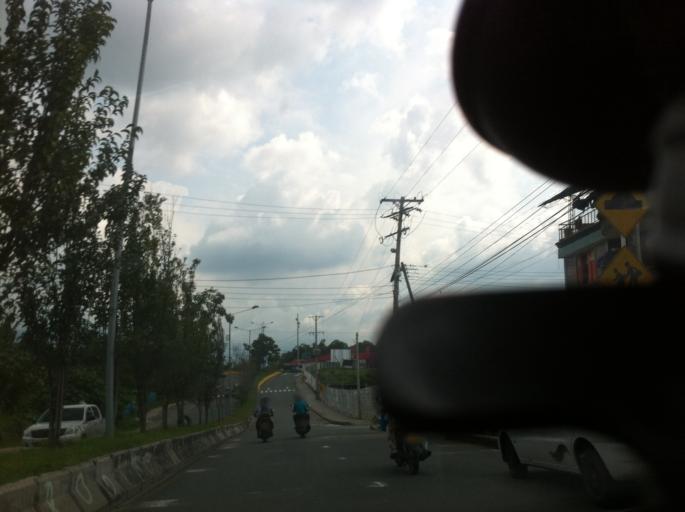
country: CO
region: Quindio
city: Armenia
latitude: 4.5139
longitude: -75.7018
